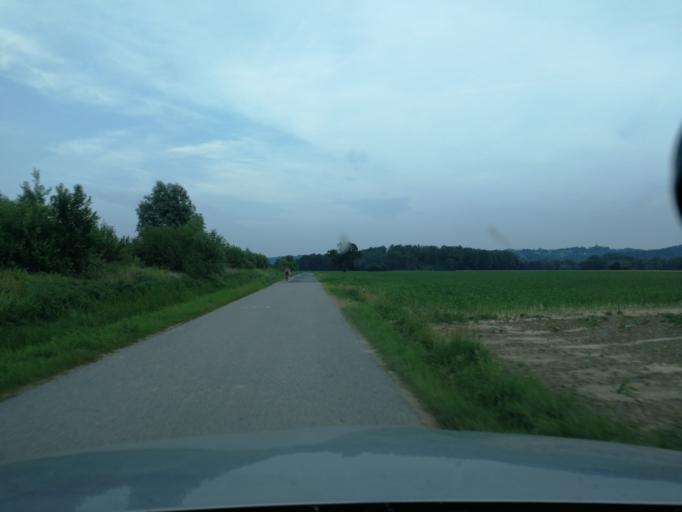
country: AT
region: Burgenland
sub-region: Politischer Bezirk Jennersdorf
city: Konigsdorf
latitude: 47.0130
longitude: 16.1544
